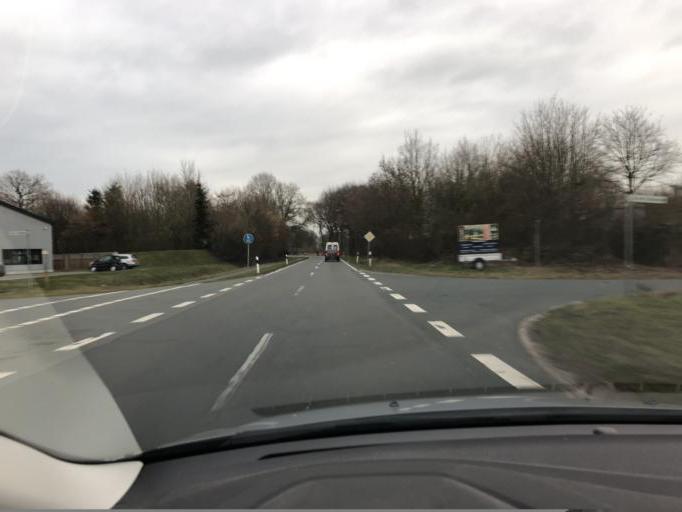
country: DE
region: Lower Saxony
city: Wiefelstede
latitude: 53.1881
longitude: 8.1180
